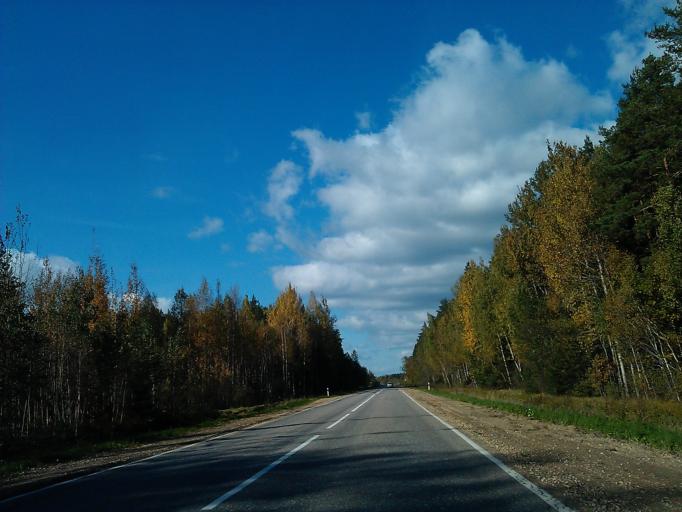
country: LV
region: Livani
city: Livani
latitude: 56.1898
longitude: 26.2970
